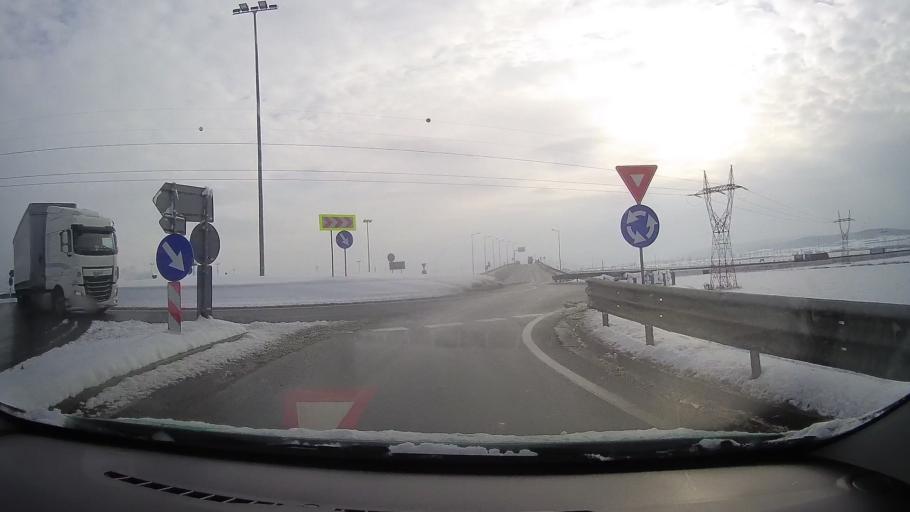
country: RO
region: Alba
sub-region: Municipiul Sebes
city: Lancram
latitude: 45.9793
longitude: 23.5198
